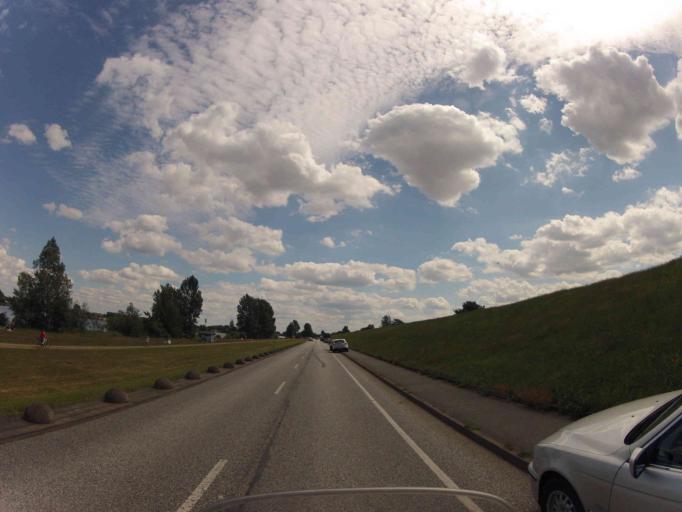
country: DE
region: Lower Saxony
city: Stelle
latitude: 53.4479
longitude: 10.0988
